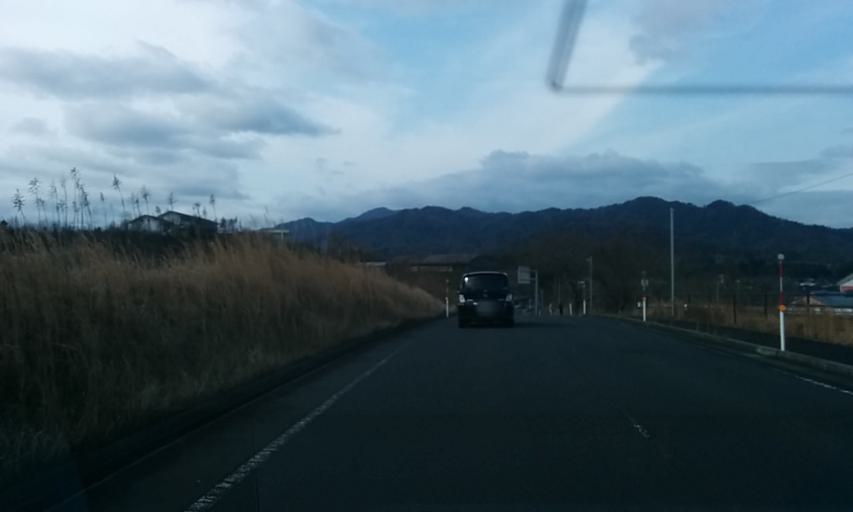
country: JP
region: Kyoto
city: Miyazu
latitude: 35.5817
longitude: 135.1045
